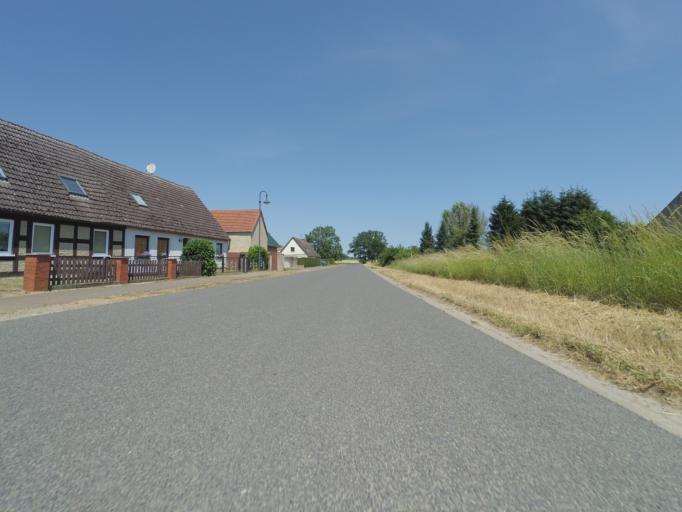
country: DE
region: Brandenburg
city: Gerdshagen
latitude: 53.2876
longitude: 12.2784
